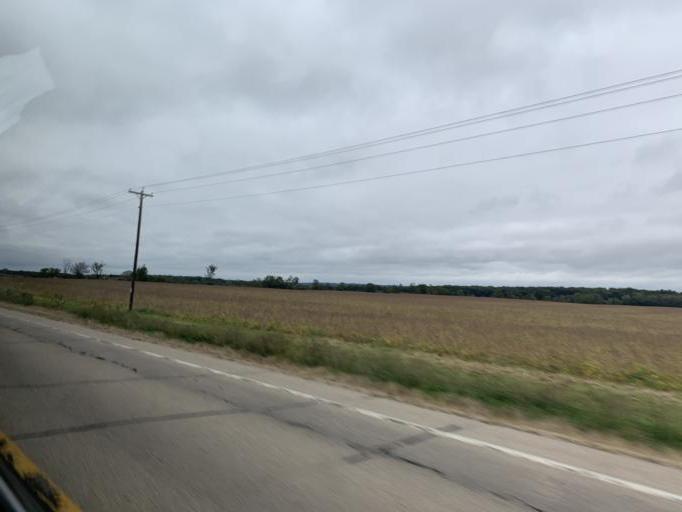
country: US
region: Wisconsin
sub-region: Grant County
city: Muscoda
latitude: 43.2198
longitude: -90.5212
